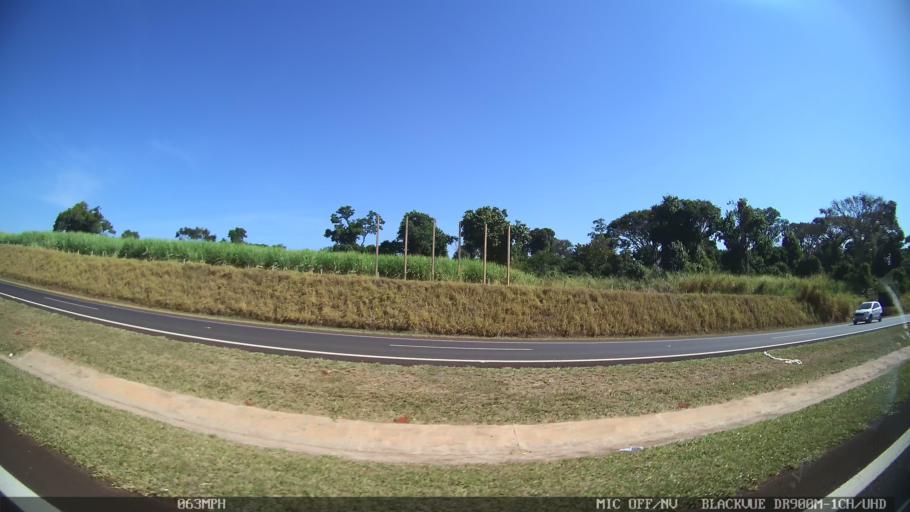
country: BR
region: Sao Paulo
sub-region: Ribeirao Preto
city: Ribeirao Preto
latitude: -21.1794
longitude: -47.8931
